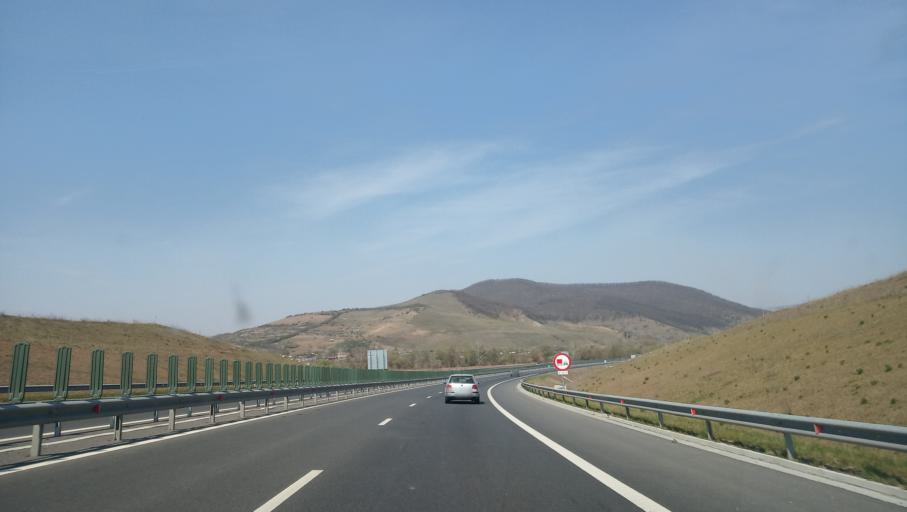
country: RO
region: Alba
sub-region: Comuna Miraslau
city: Miraslau
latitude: 46.3510
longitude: 23.7243
